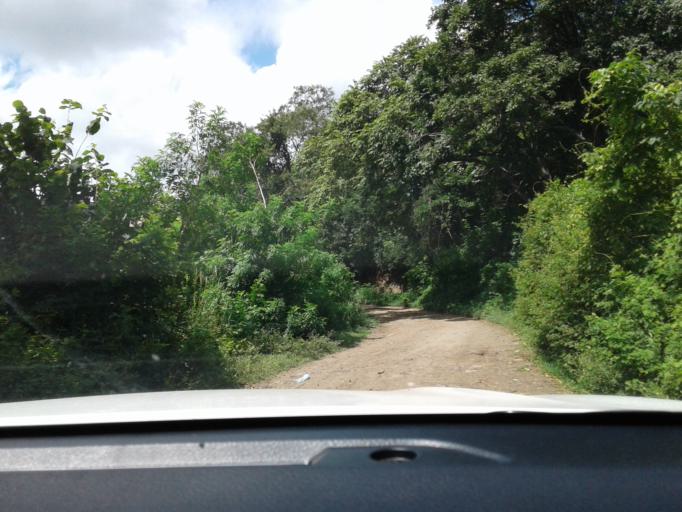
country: NI
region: Matagalpa
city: Terrabona
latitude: 12.8277
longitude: -85.9880
